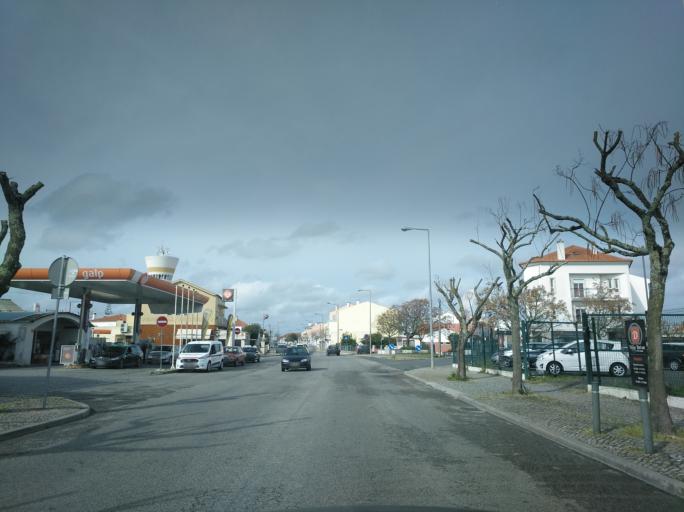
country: PT
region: Setubal
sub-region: Grandola
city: Grandola
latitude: 38.1806
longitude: -8.5671
